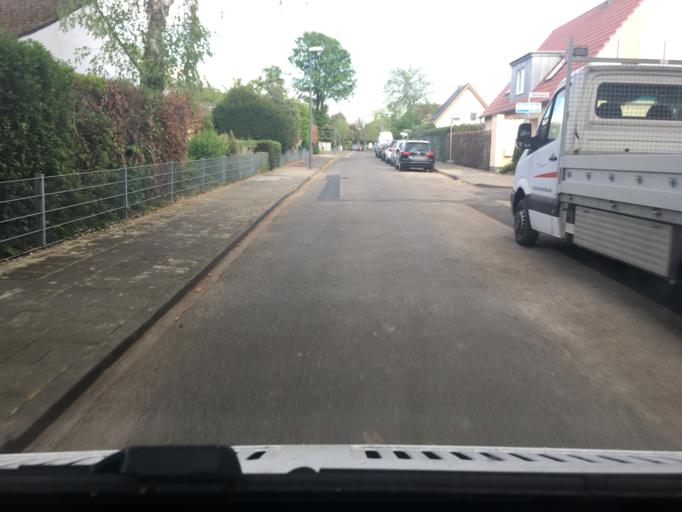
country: DE
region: North Rhine-Westphalia
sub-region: Regierungsbezirk Koln
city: Mengenich
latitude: 50.9591
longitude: 6.8746
